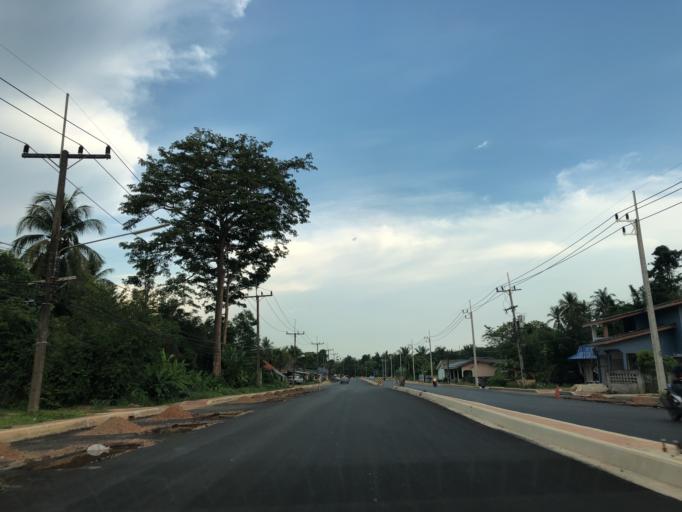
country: TH
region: Phangnga
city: Ban Ao Nang
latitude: 8.0686
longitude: 98.8419
